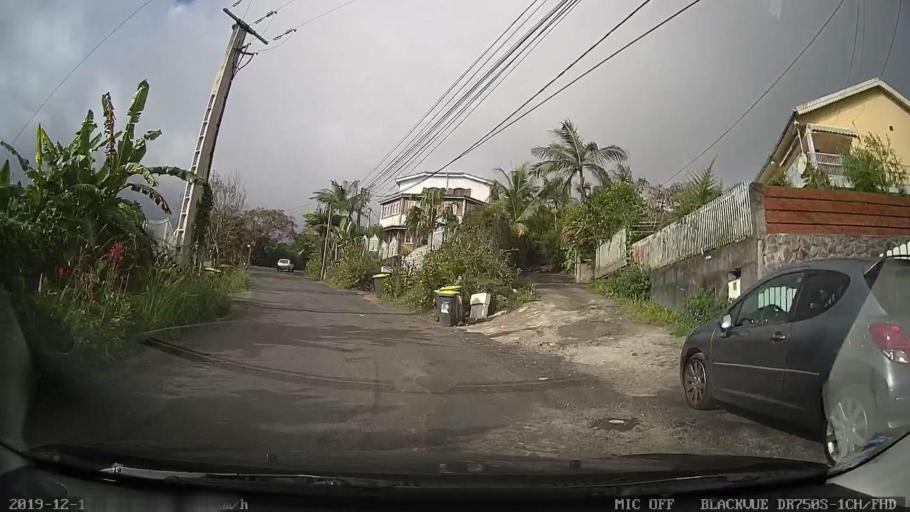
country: RE
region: Reunion
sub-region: Reunion
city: Le Tampon
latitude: -21.2558
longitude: 55.5164
